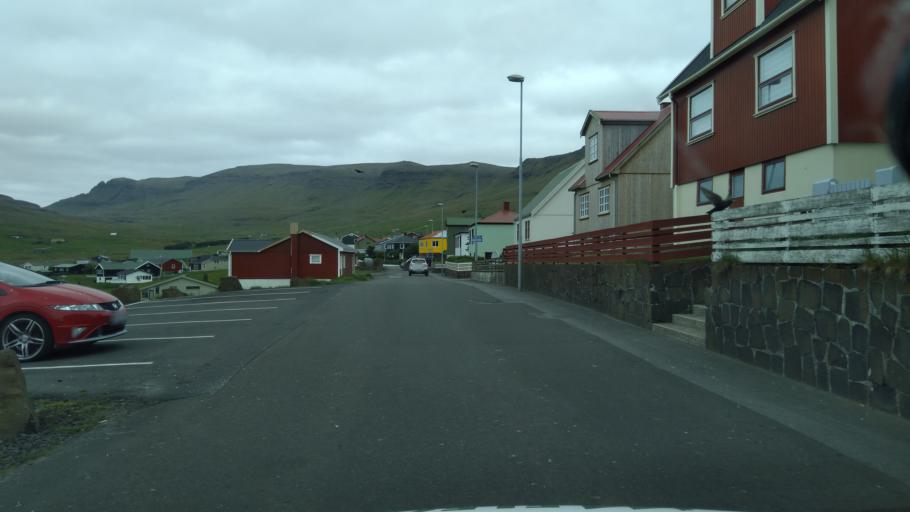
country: FO
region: Suduroy
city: Tvoroyri
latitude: 61.5627
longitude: -6.8348
